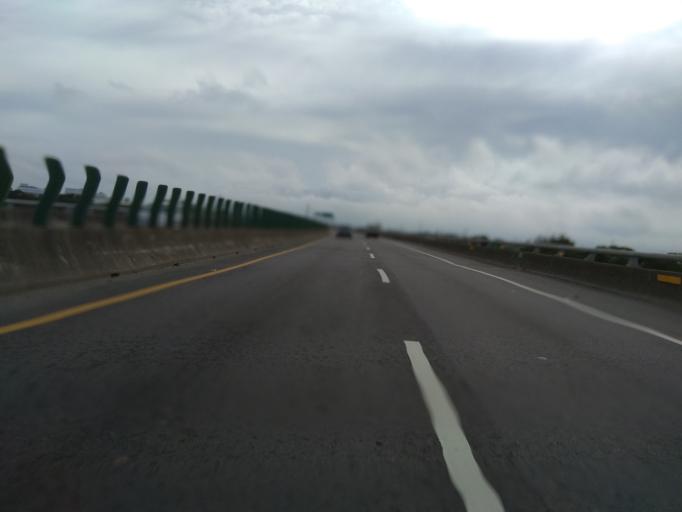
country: TW
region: Taiwan
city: Daxi
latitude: 24.9004
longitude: 121.2397
